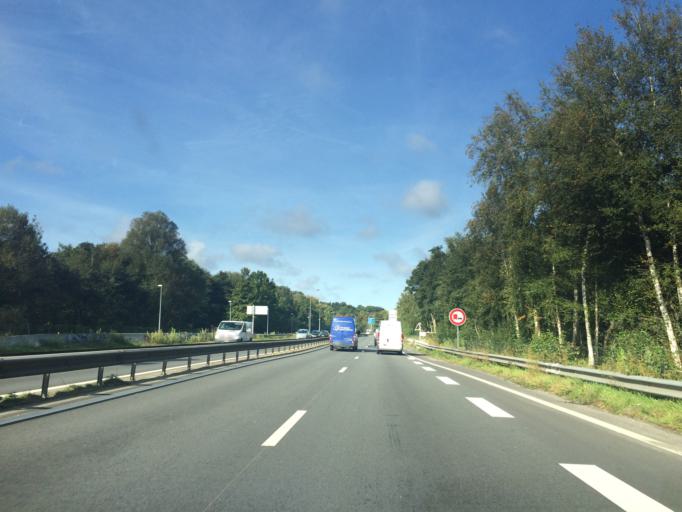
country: FR
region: Pays de la Loire
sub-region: Departement de la Loire-Atlantique
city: La Chapelle-sur-Erdre
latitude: 47.2575
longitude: -1.5500
